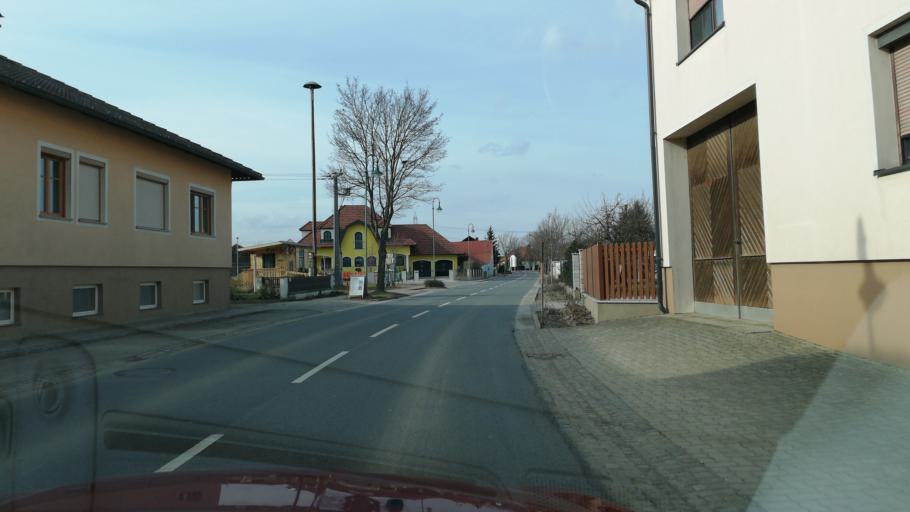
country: AT
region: Lower Austria
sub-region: Politischer Bezirk Tulln
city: Atzenbrugg
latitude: 48.3135
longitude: 15.8722
